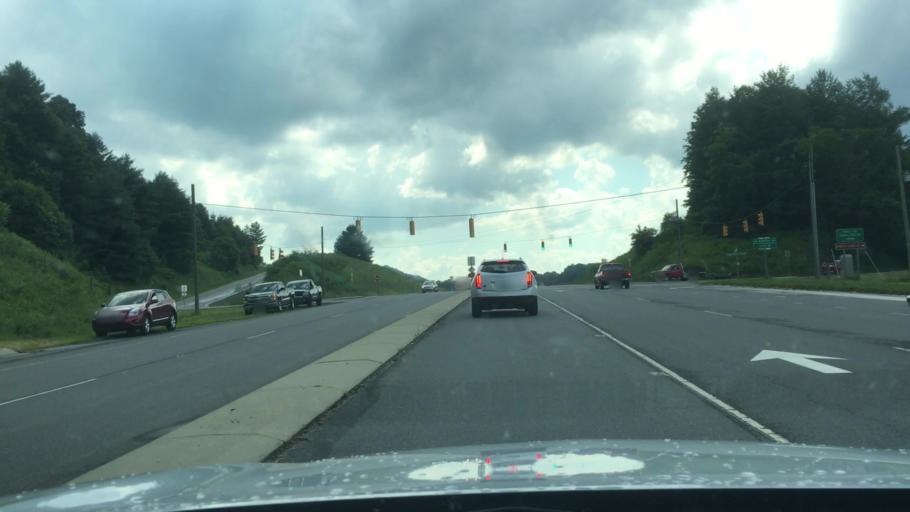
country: US
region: North Carolina
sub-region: Yancey County
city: Burnsville
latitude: 35.9106
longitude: -82.3568
